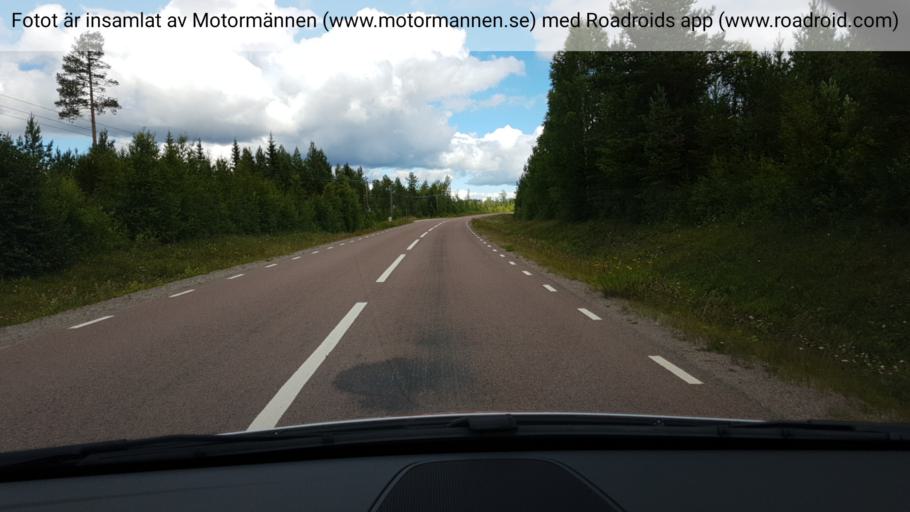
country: SE
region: Jaemtland
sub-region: Braecke Kommun
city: Braecke
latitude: 62.9243
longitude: 15.6790
